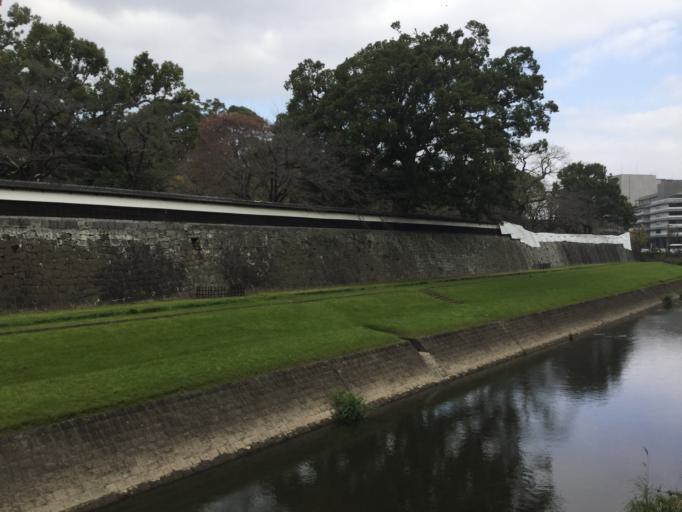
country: JP
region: Kumamoto
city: Kumamoto
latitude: 32.8031
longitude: 130.7058
